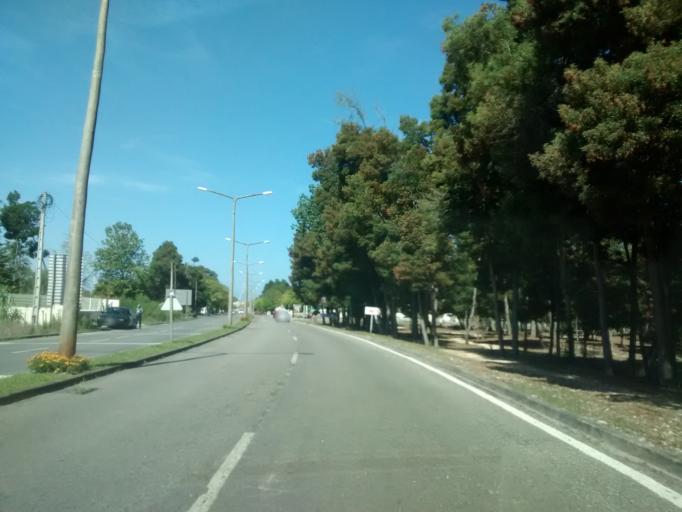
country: PT
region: Coimbra
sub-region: Mira
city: Mira
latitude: 40.4547
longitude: -8.7808
